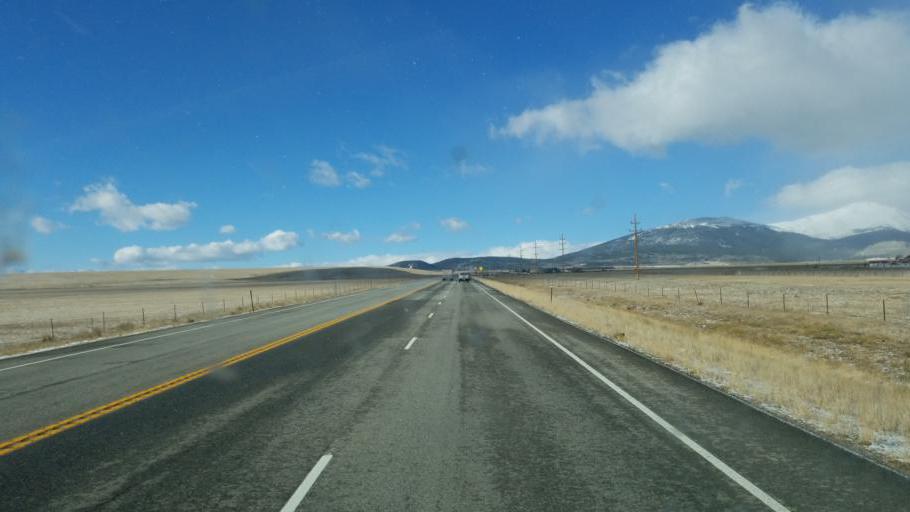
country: US
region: Colorado
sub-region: Park County
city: Fairplay
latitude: 39.3470
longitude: -105.8393
